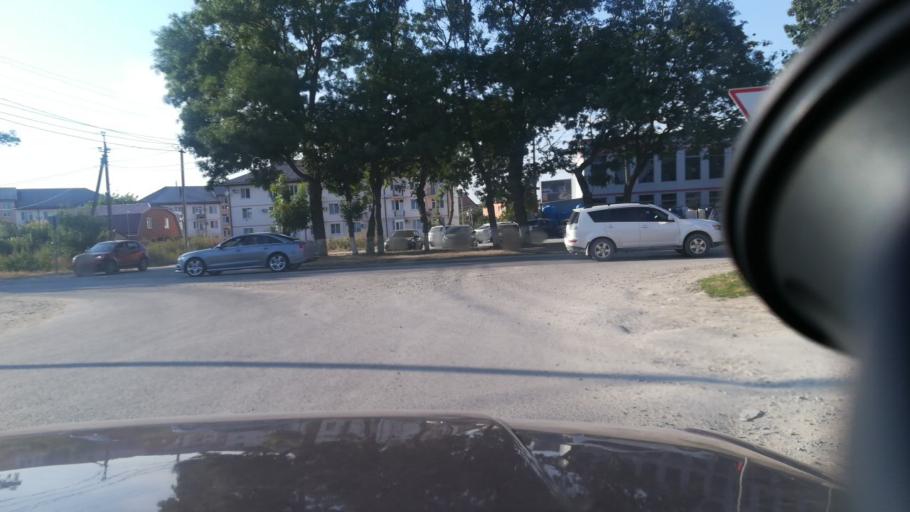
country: RU
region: Krasnodarskiy
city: Vityazevo
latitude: 45.0017
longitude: 37.2922
